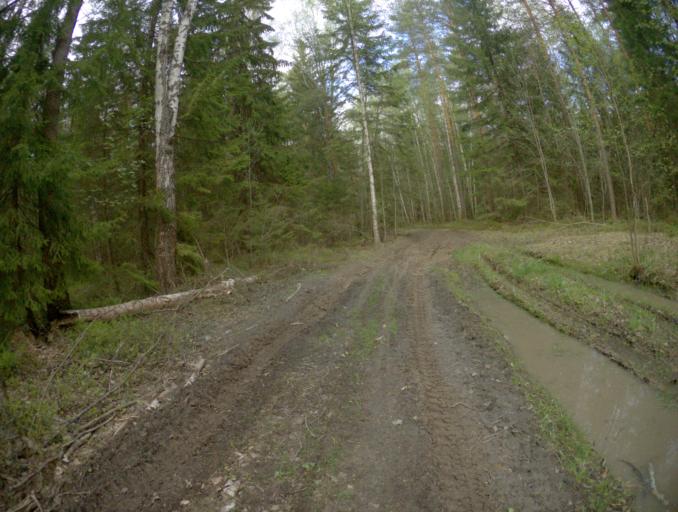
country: RU
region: Vladimir
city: Golovino
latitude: 55.9131
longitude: 40.4971
